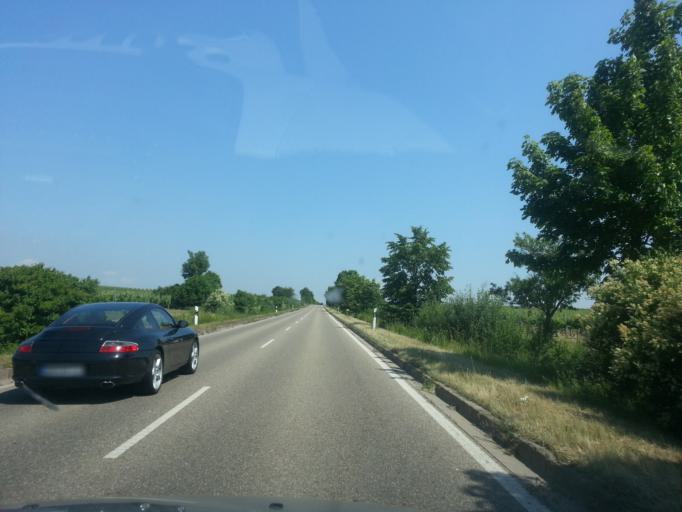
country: DE
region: Rheinland-Pfalz
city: Kallstadt
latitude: 49.4836
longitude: 8.1887
